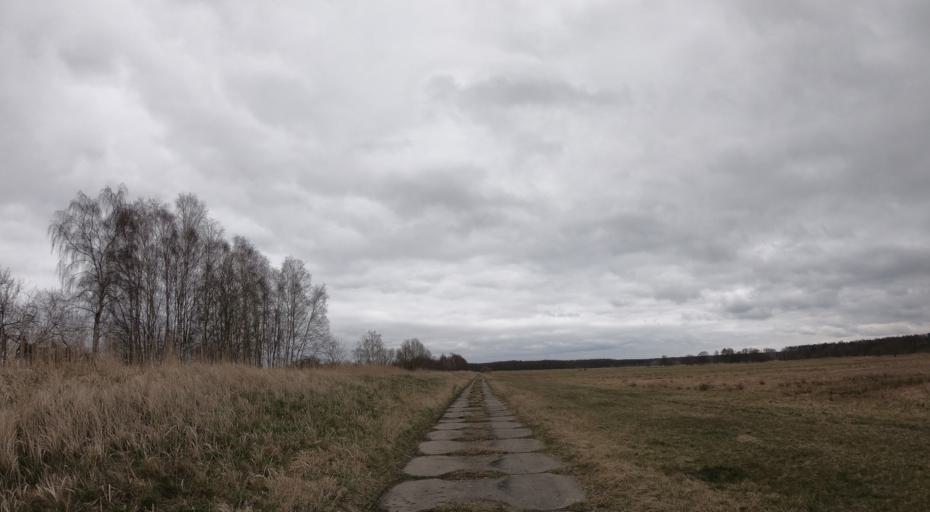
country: PL
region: West Pomeranian Voivodeship
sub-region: Powiat policki
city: Nowe Warpno
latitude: 53.6902
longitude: 14.3837
